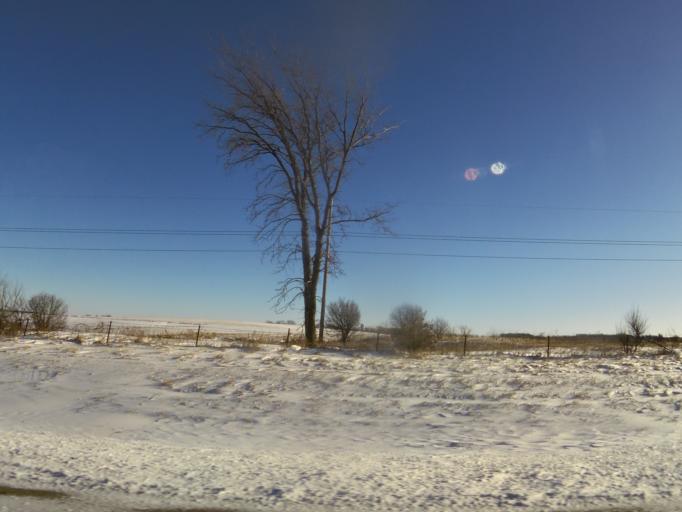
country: US
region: Minnesota
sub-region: Rice County
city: Faribault
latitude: 44.2513
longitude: -93.2850
